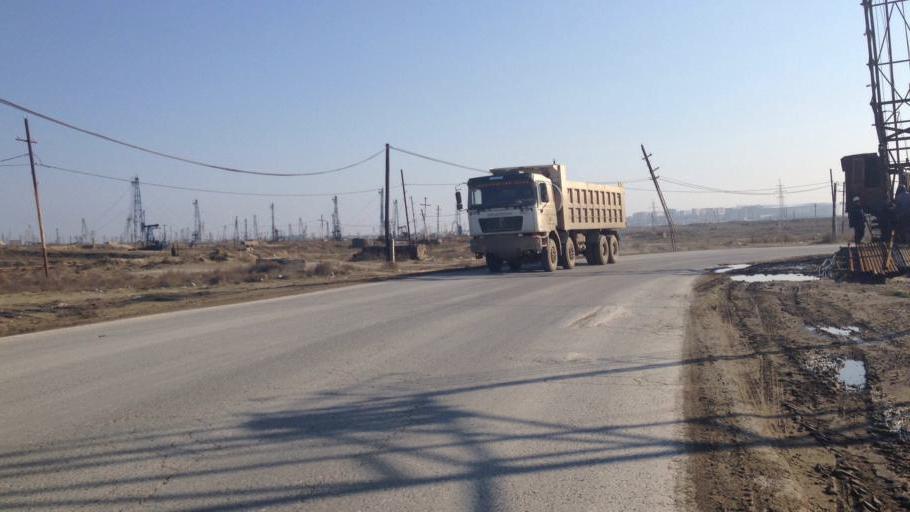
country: AZ
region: Baki
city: Balakhani
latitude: 40.4563
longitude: 49.8936
